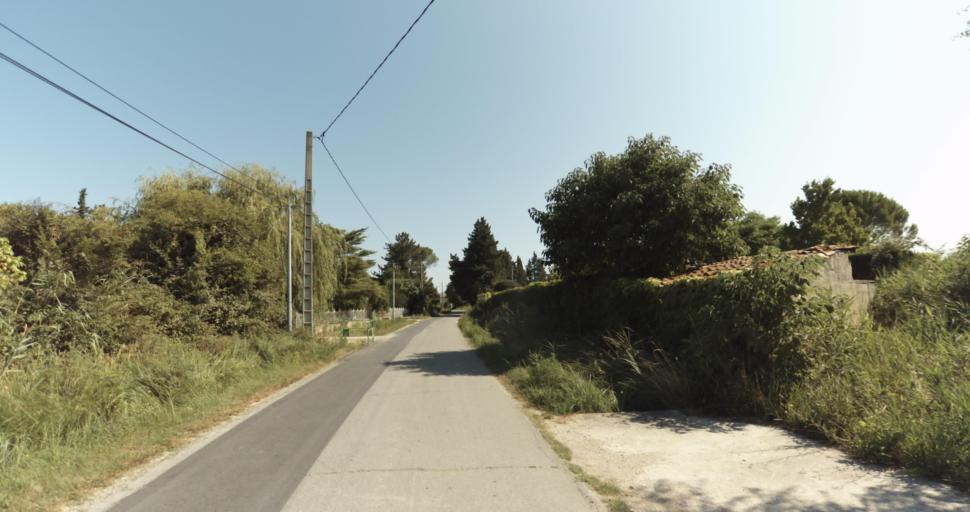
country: FR
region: Provence-Alpes-Cote d'Azur
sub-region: Departement du Vaucluse
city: Monteux
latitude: 44.0225
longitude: 4.9917
